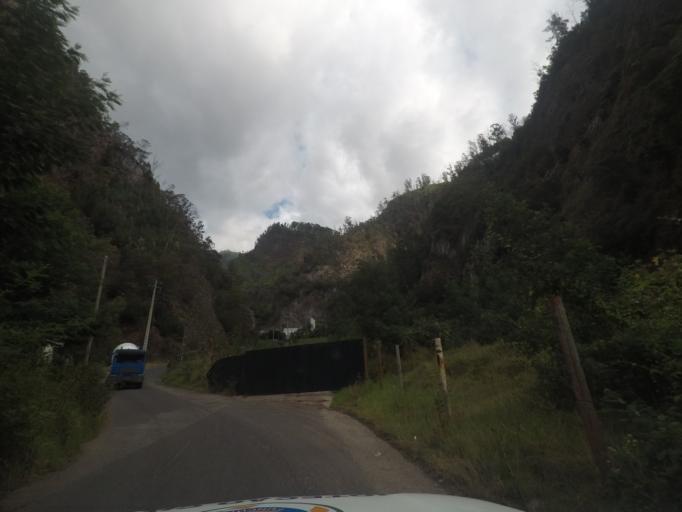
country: PT
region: Madeira
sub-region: Funchal
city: Nossa Senhora do Monte
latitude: 32.6816
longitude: -16.9154
